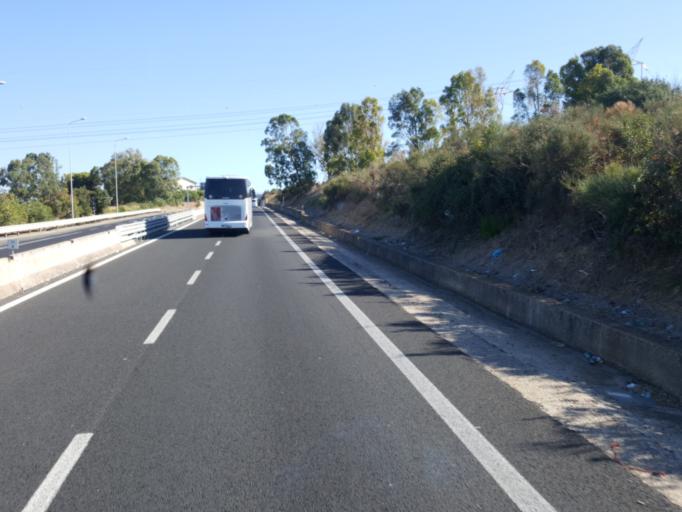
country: IT
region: Latium
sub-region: Citta metropolitana di Roma Capitale
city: Aurelia
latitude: 42.1303
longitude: 11.7931
